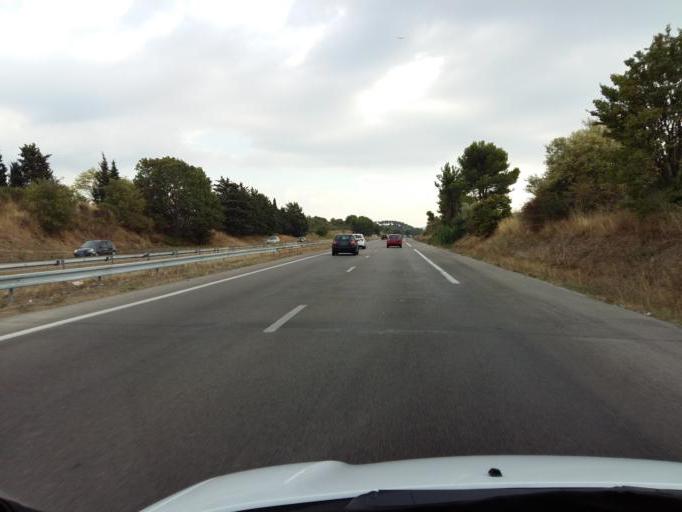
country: FR
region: Provence-Alpes-Cote d'Azur
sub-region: Departement des Bouches-du-Rhone
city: Bouc-Bel-Air
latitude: 43.4839
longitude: 5.4080
